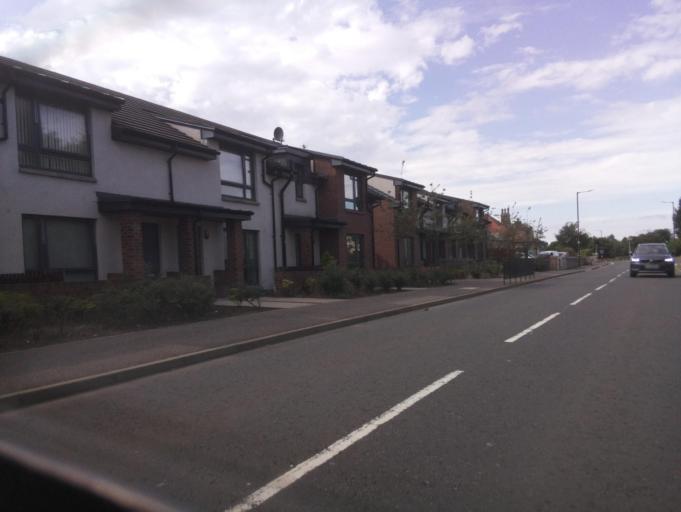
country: GB
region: Scotland
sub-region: East Lothian
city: Cockenzie
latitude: 55.9677
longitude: -2.9597
